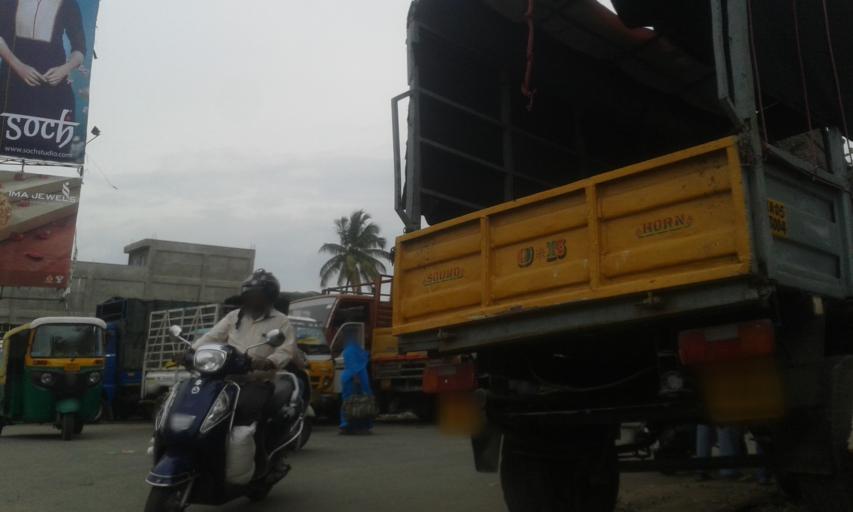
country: IN
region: Karnataka
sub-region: Bangalore Urban
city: Bangalore
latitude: 12.9501
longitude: 77.6033
